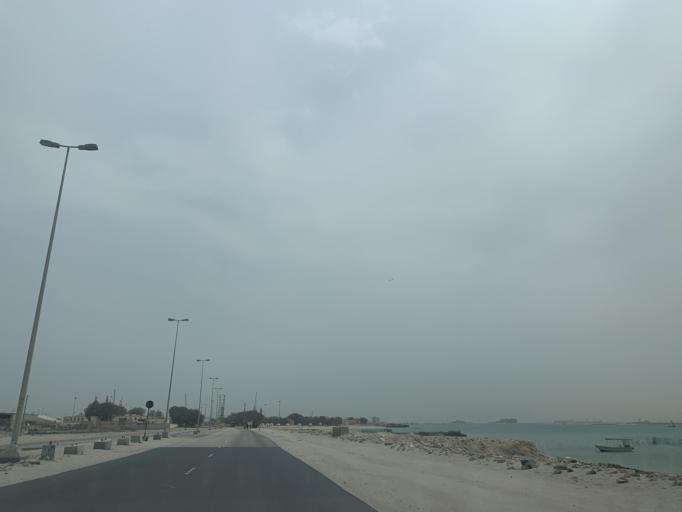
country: BH
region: Muharraq
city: Al Hadd
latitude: 26.2016
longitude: 50.6610
